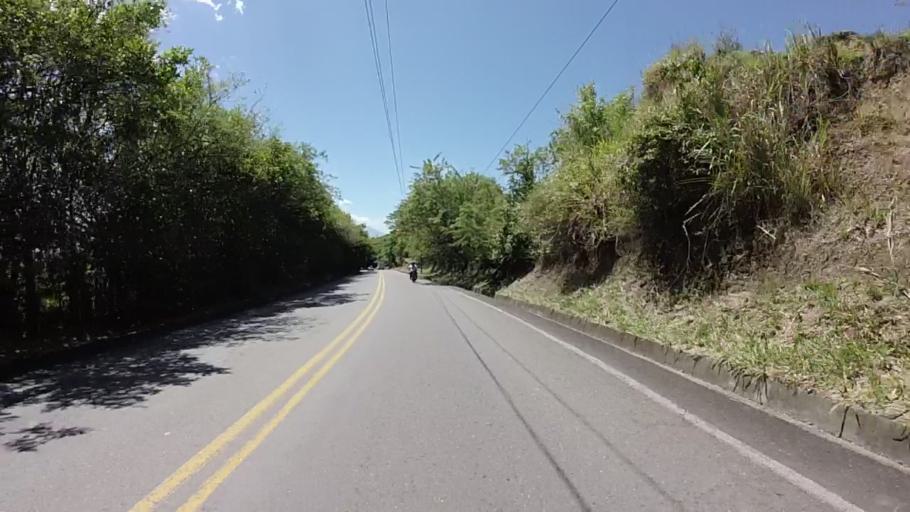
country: CO
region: Valle del Cauca
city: Cartago
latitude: 4.7286
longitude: -75.8928
